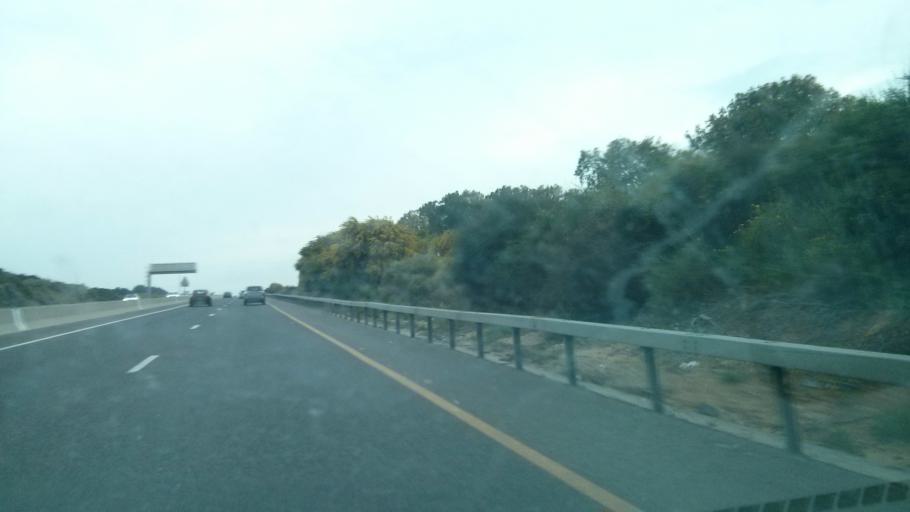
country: IL
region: Haifa
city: Hadera
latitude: 32.4647
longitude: 34.8964
